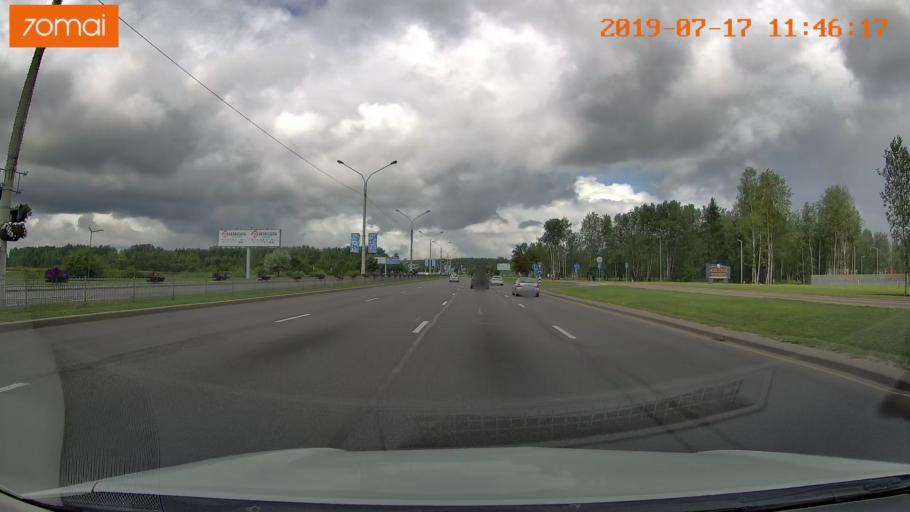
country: BY
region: Minsk
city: Zhdanovichy
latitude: 53.9471
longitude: 27.4567
